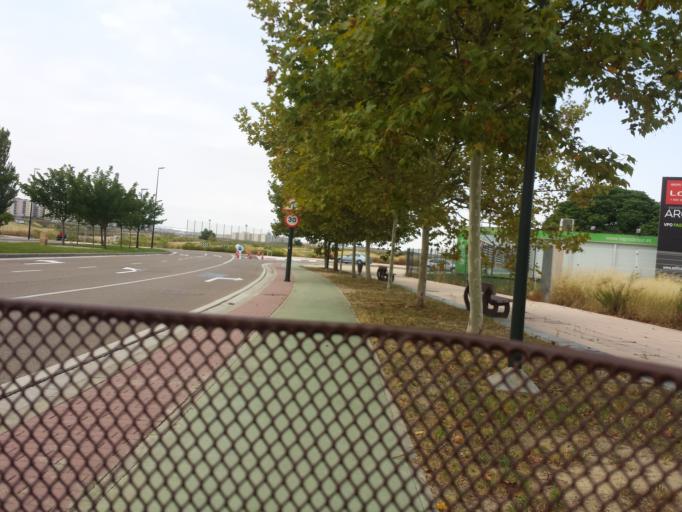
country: ES
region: Aragon
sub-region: Provincia de Zaragoza
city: Montecanal
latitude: 41.6245
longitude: -0.9408
